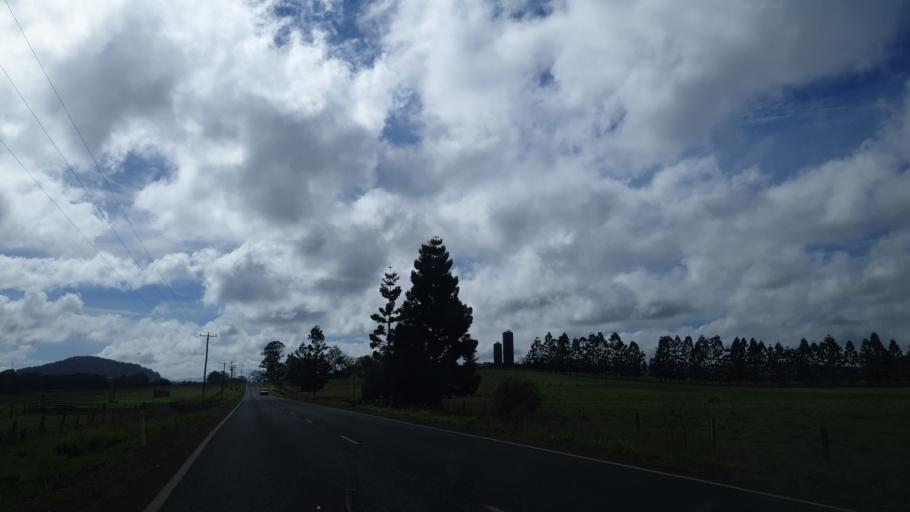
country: AU
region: Queensland
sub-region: Tablelands
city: Atherton
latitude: -17.2953
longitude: 145.5360
